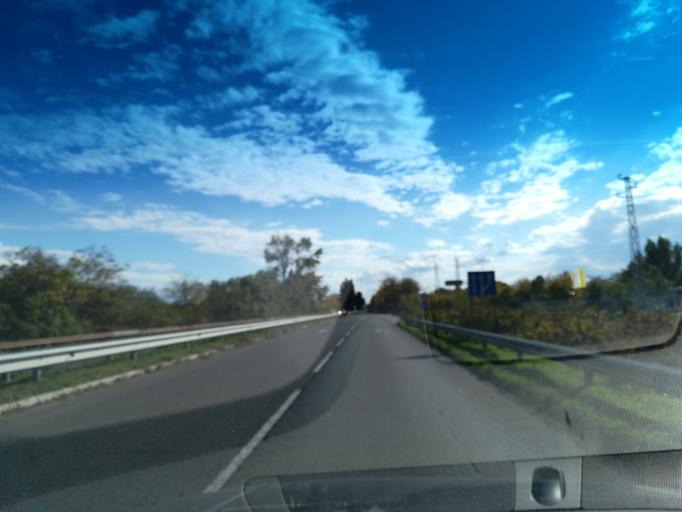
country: BG
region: Stara Zagora
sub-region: Obshtina Stara Zagora
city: Stara Zagora
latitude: 42.3896
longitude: 25.6473
